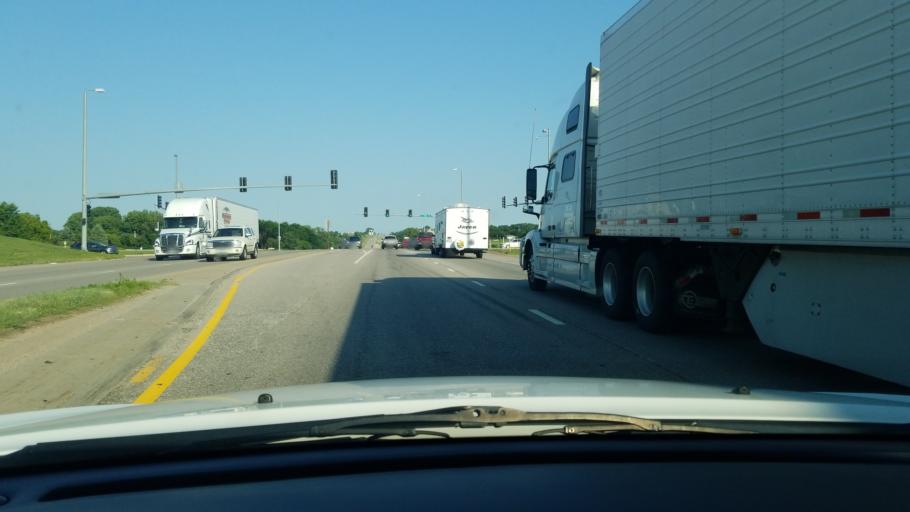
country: US
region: Nebraska
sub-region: Lancaster County
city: Lincoln
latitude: 40.7464
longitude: -96.6259
